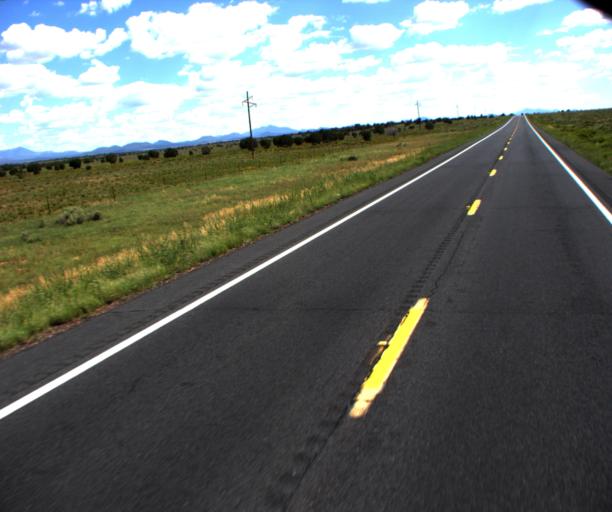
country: US
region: Arizona
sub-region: Coconino County
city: Grand Canyon Village
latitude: 35.6987
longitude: -112.1331
